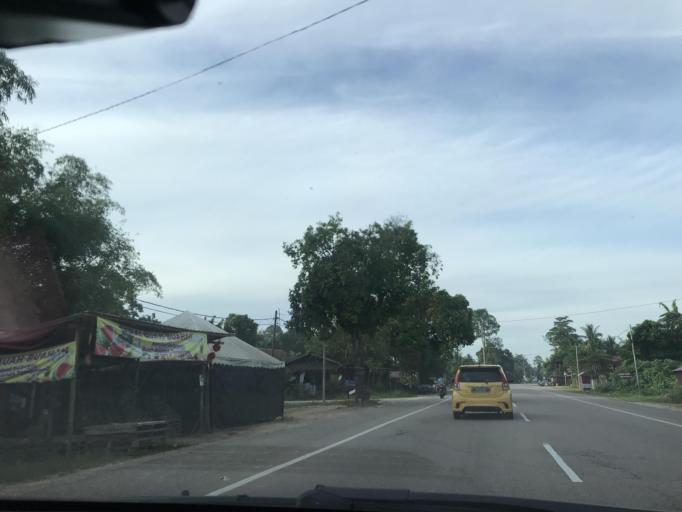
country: MY
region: Kelantan
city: Ketereh
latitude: 5.9722
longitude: 102.1928
